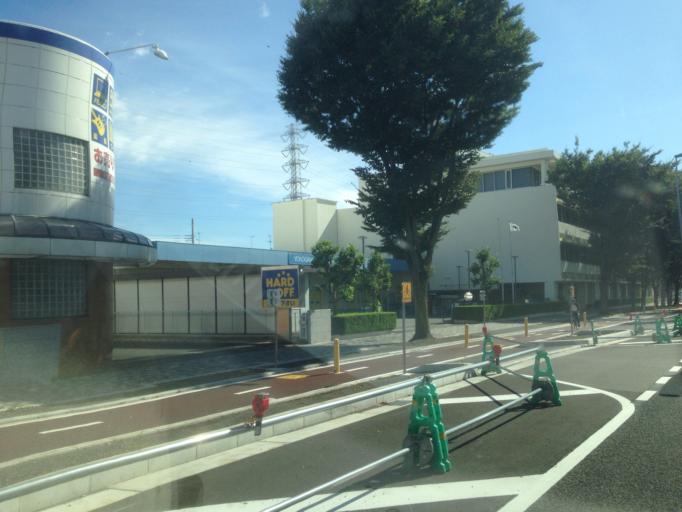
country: JP
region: Tokyo
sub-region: Machida-shi
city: Machida
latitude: 35.5715
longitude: 139.3772
